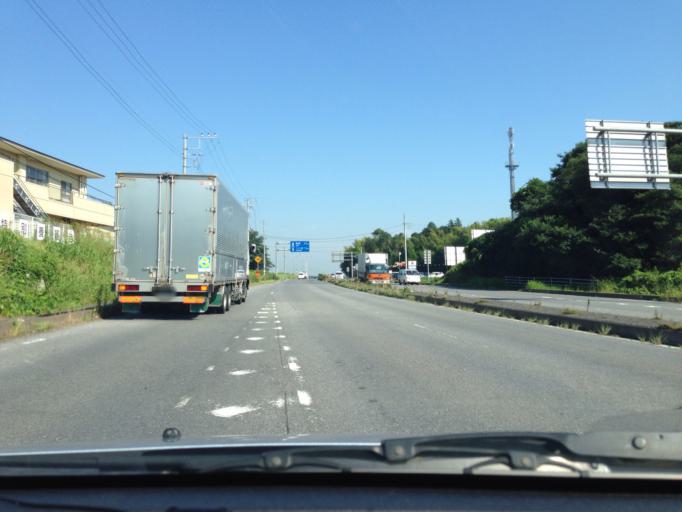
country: JP
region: Ibaraki
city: Naka
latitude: 36.0506
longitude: 140.1843
